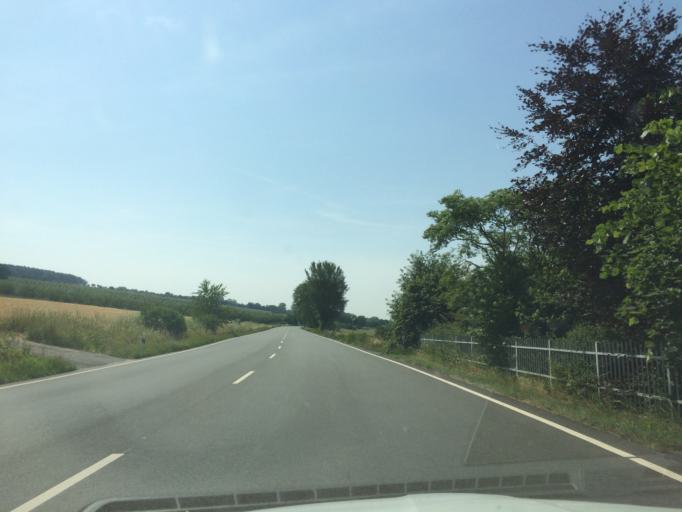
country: DE
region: Hesse
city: Trendelburg
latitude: 51.5597
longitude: 9.4152
